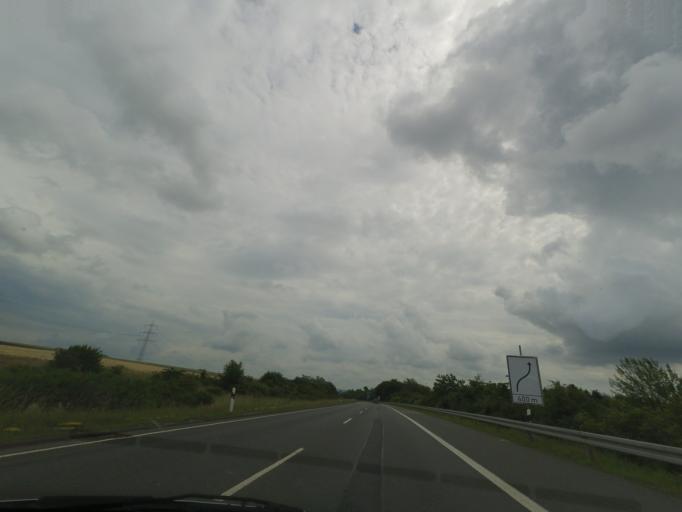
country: DE
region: Hesse
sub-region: Regierungsbezirk Giessen
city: Heuchelheim
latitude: 50.6049
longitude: 8.6363
